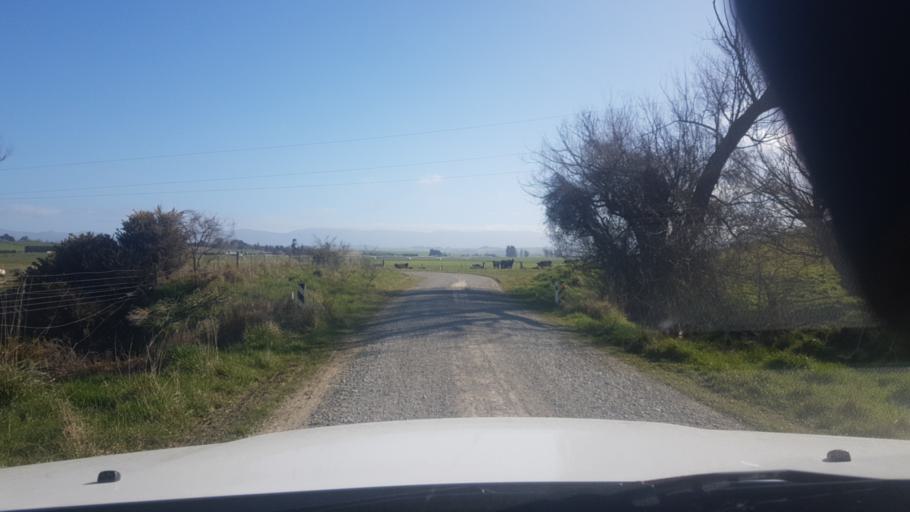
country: NZ
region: Canterbury
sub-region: Timaru District
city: Timaru
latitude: -44.4272
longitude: 171.1521
